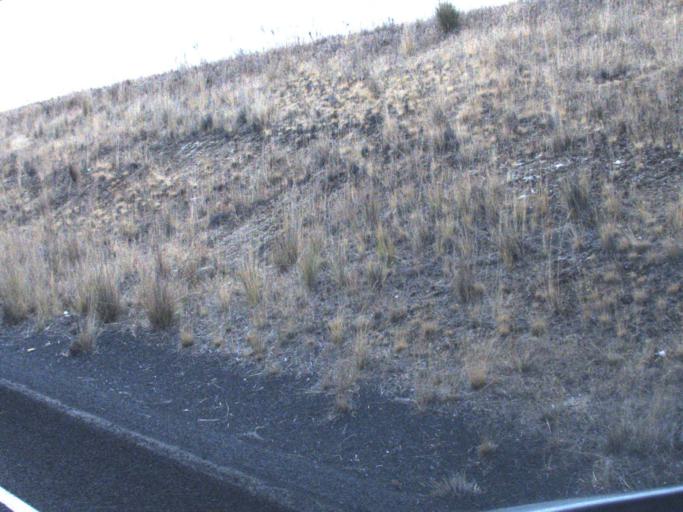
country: US
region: Washington
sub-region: Okanogan County
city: Coulee Dam
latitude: 47.8440
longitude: -118.8074
